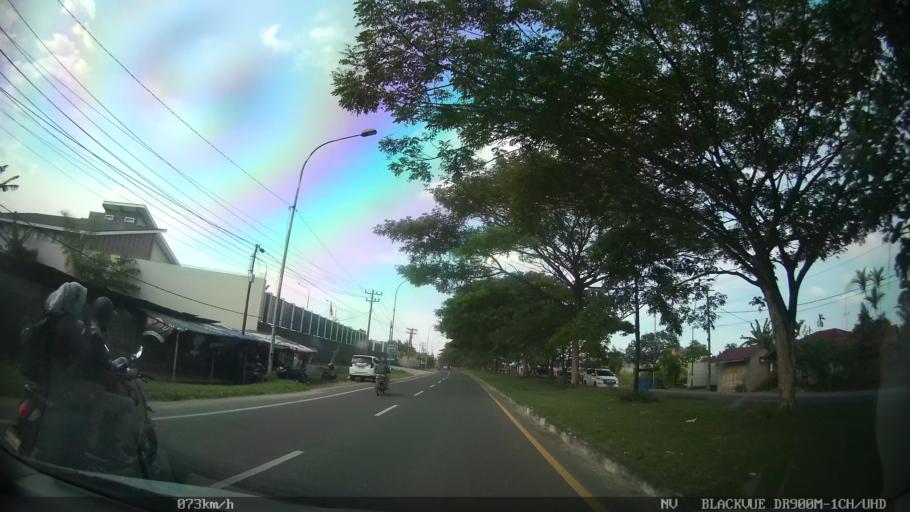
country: ID
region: North Sumatra
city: Percut
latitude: 3.5677
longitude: 98.7956
